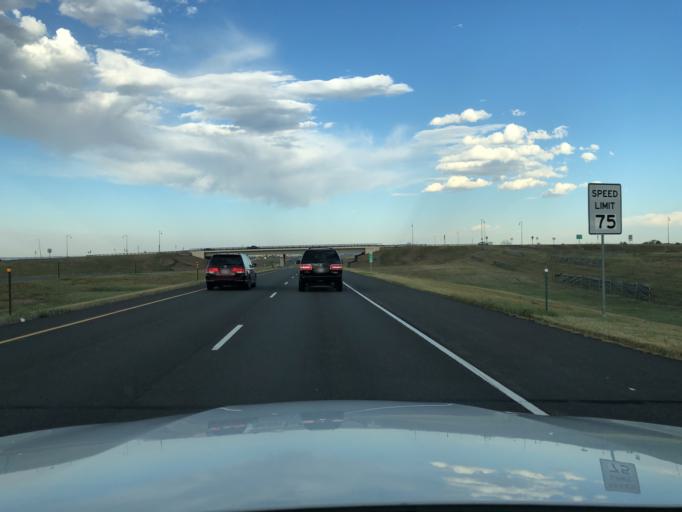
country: US
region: Colorado
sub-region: Boulder County
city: Lafayette
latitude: 39.9838
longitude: -105.0219
